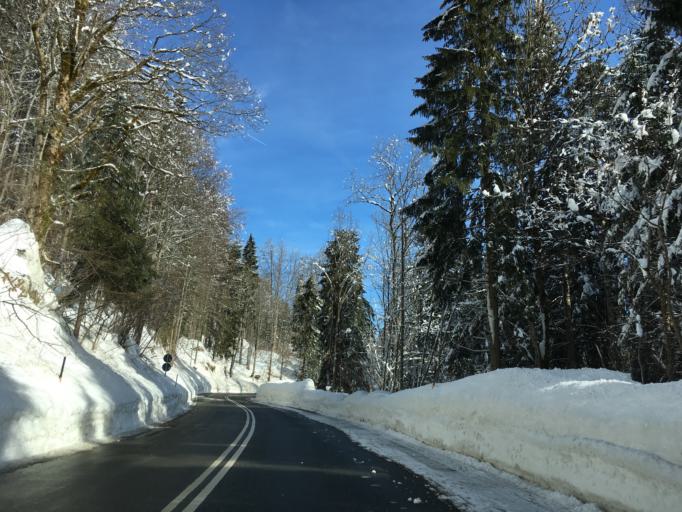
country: DE
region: Bavaria
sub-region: Upper Bavaria
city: Burg Unter-Falkenstein
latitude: 47.6713
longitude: 12.0753
